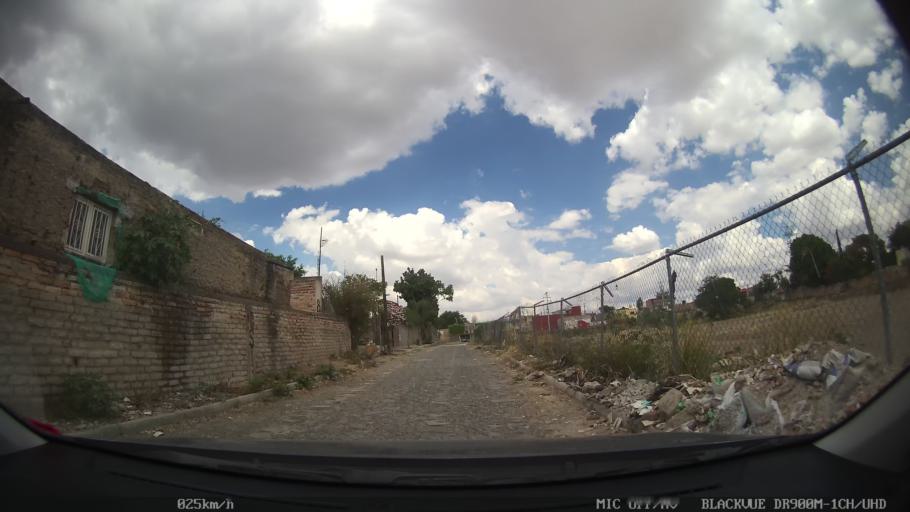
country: MX
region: Jalisco
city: Tlaquepaque
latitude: 20.6741
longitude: -103.2633
